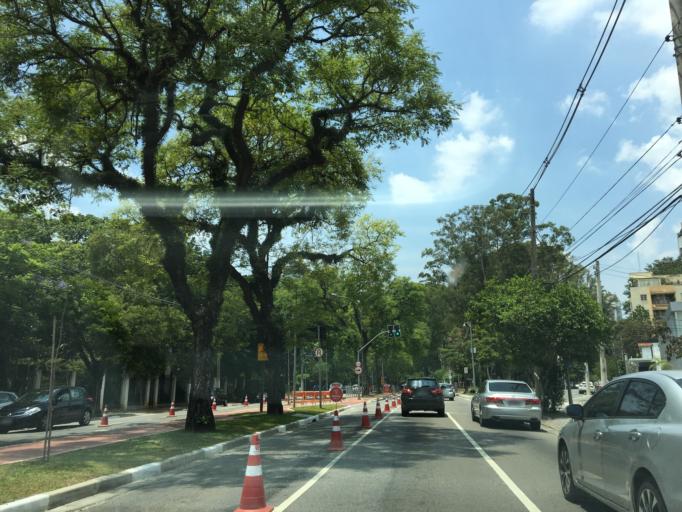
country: BR
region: Sao Paulo
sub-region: Sao Paulo
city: Sao Paulo
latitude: -23.5917
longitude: -46.6648
